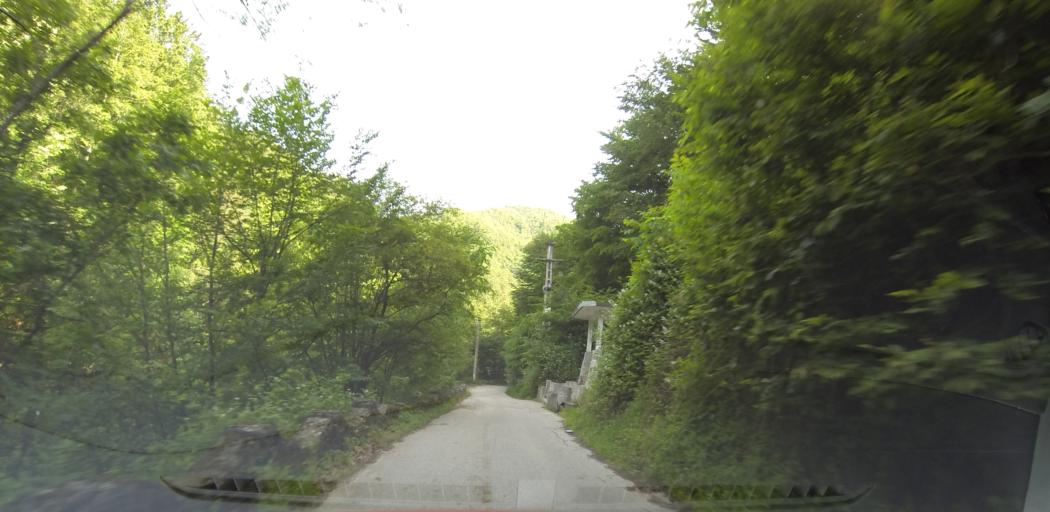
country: RO
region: Valcea
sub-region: Oras Baile Olanesti
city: Baile Olanesti
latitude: 45.2080
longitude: 24.2341
